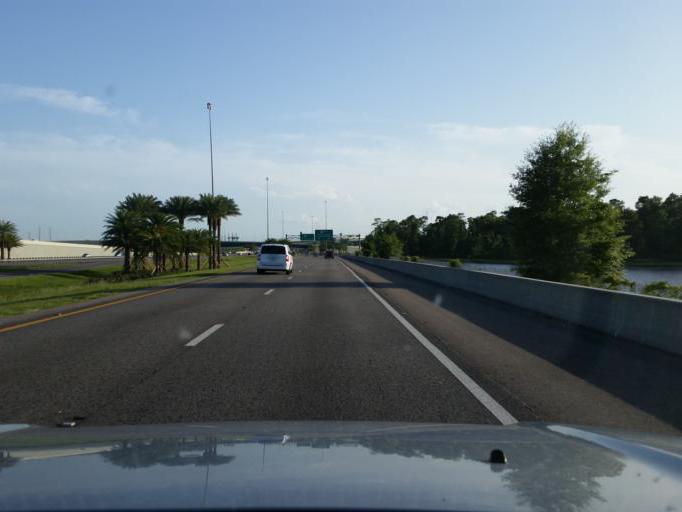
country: US
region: Florida
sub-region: Osceola County
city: Celebration
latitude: 28.3387
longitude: -81.5407
